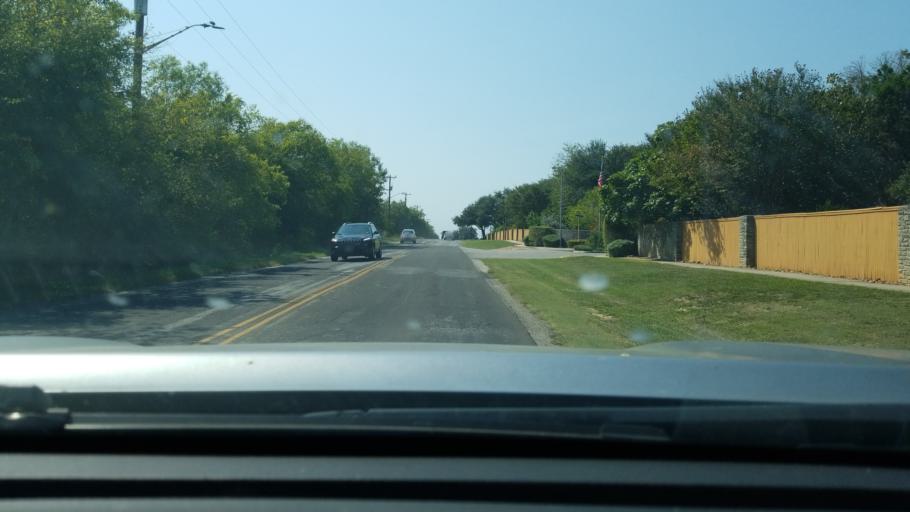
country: US
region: Texas
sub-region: Bexar County
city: Leon Valley
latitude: 29.5447
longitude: -98.6092
